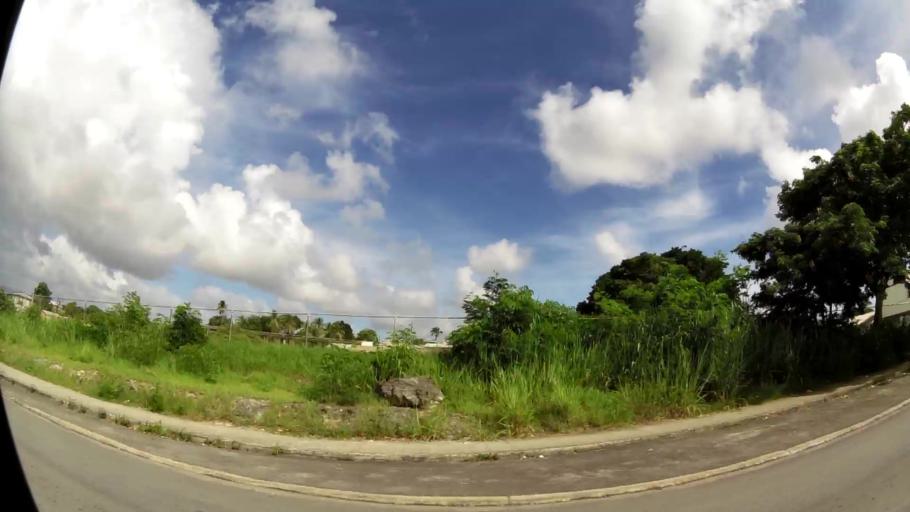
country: BB
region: Saint Michael
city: Bridgetown
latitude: 13.0958
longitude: -59.5932
